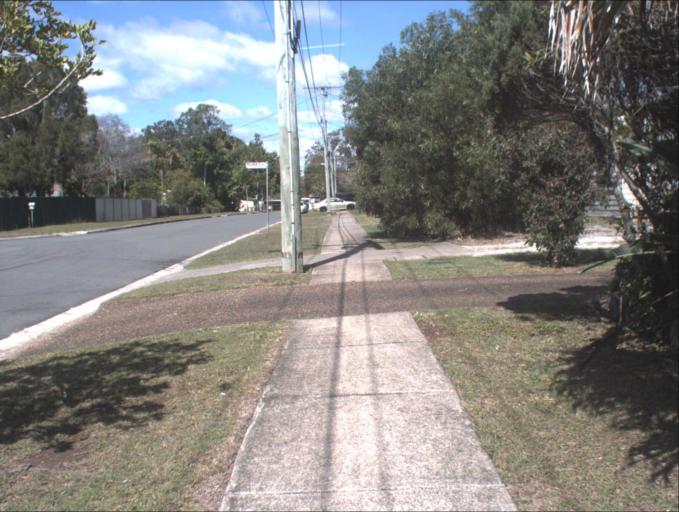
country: AU
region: Queensland
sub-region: Logan
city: Waterford West
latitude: -27.6728
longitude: 153.1069
